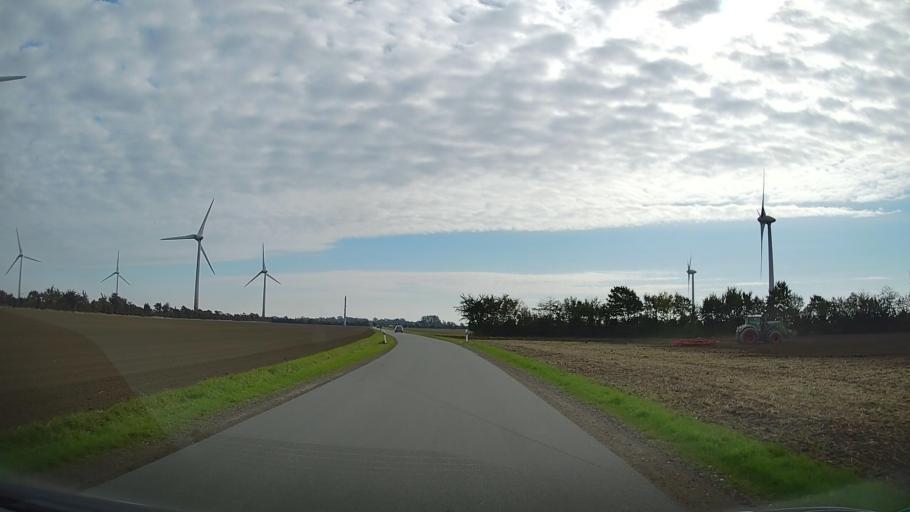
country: DE
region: Schleswig-Holstein
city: Grossenbrode
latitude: 54.5120
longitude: 11.0545
